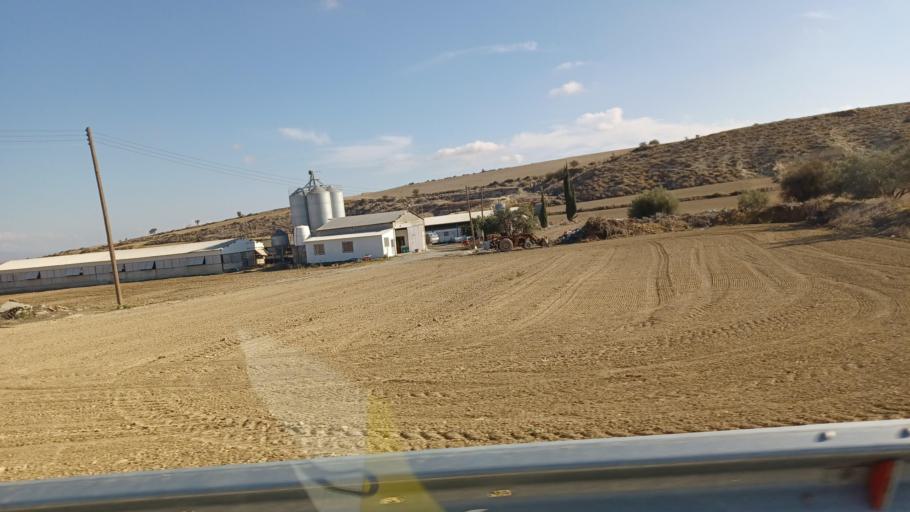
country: CY
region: Larnaka
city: Athienou
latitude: 35.0434
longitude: 33.5556
